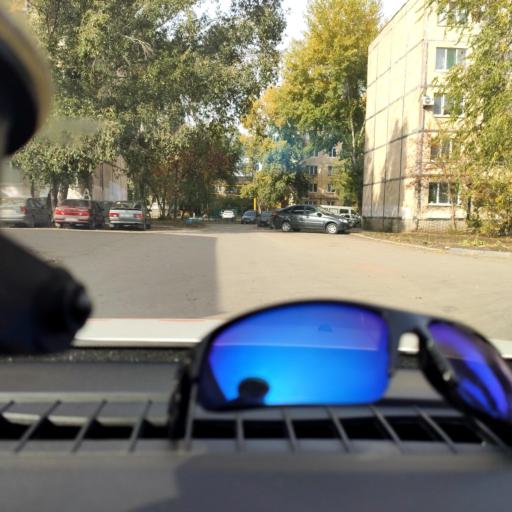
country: RU
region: Samara
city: Samara
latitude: 53.1203
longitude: 50.0917
